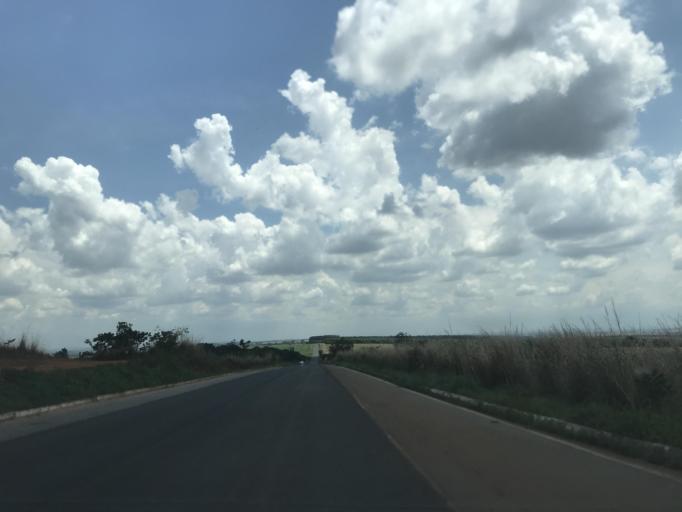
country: BR
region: Goias
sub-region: Piracanjuba
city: Piracanjuba
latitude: -17.3461
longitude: -48.7932
